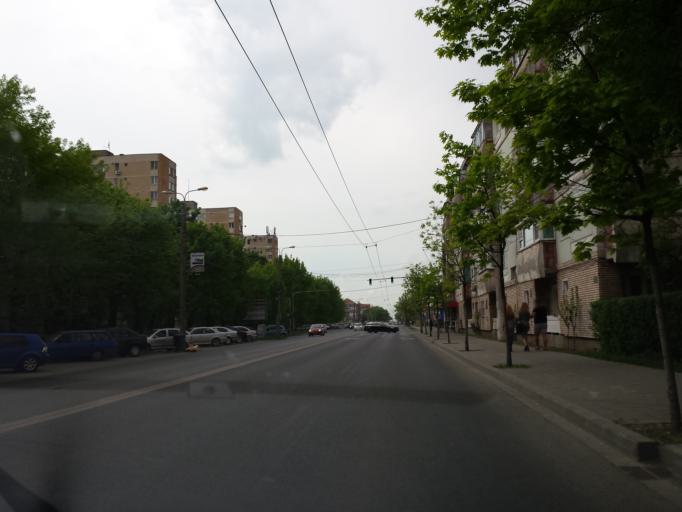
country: RO
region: Timis
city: Timisoara
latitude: 45.7668
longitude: 21.2225
